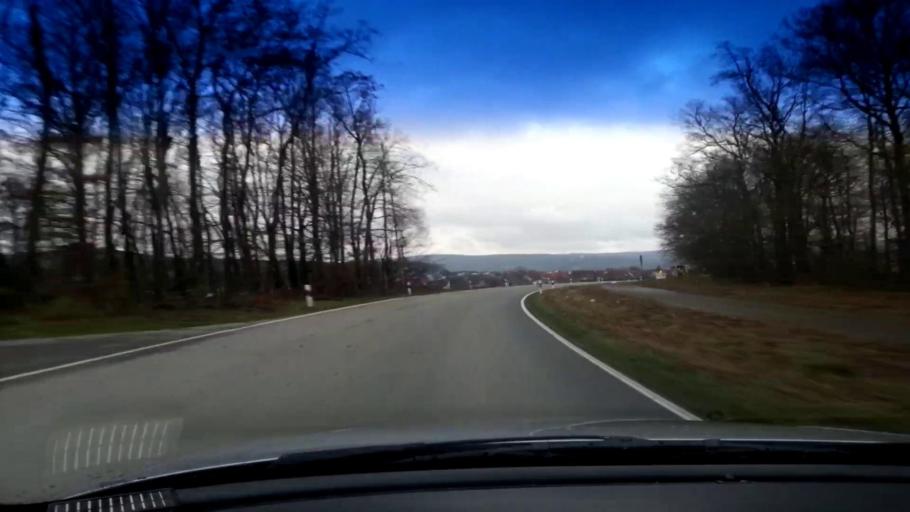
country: DE
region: Bavaria
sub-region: Upper Franconia
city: Litzendorf
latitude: 49.9298
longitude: 10.9996
